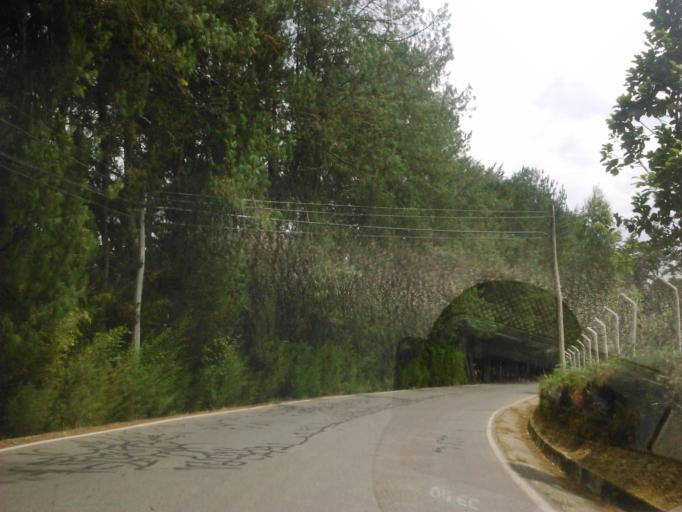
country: CO
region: Antioquia
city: San Vicente
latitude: 6.2349
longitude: -75.3772
